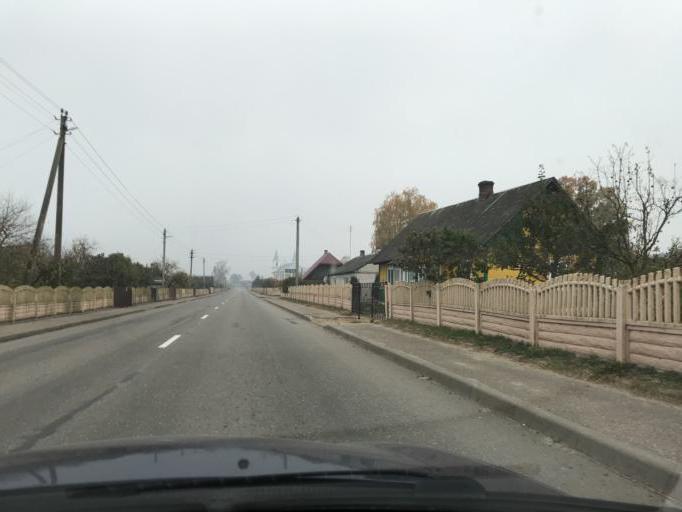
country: BY
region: Grodnenskaya
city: Hrodna
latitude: 53.8192
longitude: 23.8671
